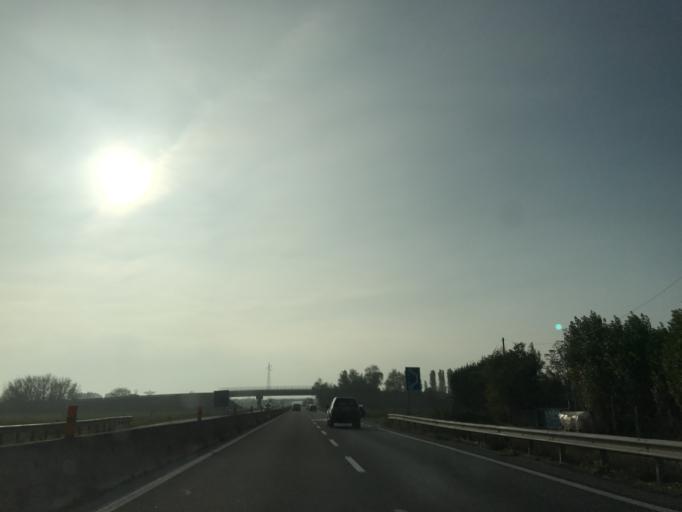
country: IT
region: Emilia-Romagna
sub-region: Provincia di Rimini
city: Bellaria-Igea Marina
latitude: 44.1385
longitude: 12.4602
